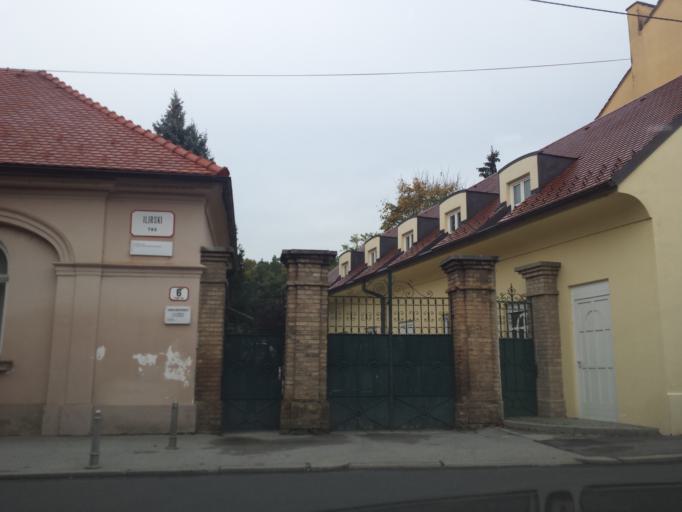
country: HR
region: Grad Zagreb
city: Zagreb
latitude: 45.8194
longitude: 15.9752
